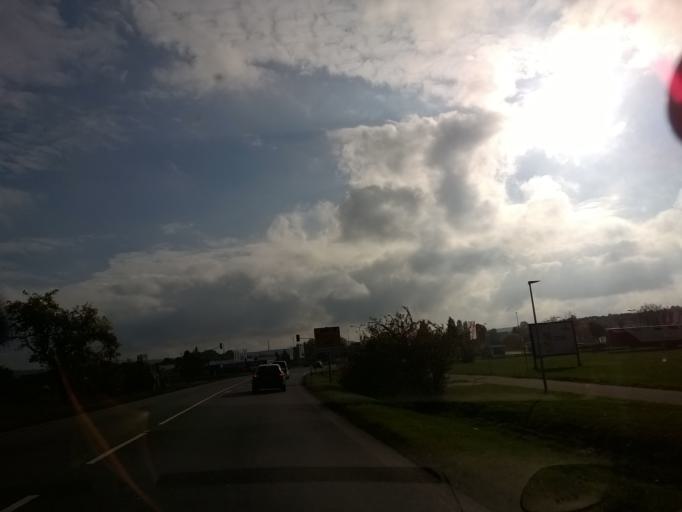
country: DE
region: Thuringia
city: Nordhausen
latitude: 51.4745
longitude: 10.8100
